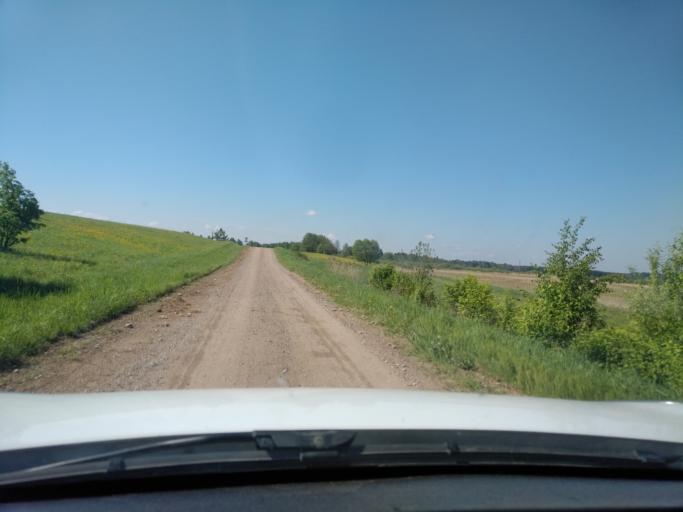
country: LT
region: Panevezys
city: Rokiskis
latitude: 55.7809
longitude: 25.7616
